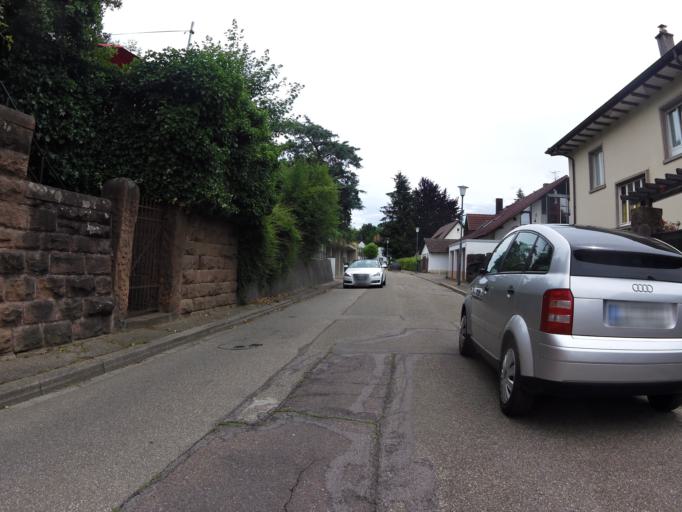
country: DE
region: Baden-Wuerttemberg
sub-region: Freiburg Region
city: Lahr
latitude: 48.3413
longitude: 7.8898
